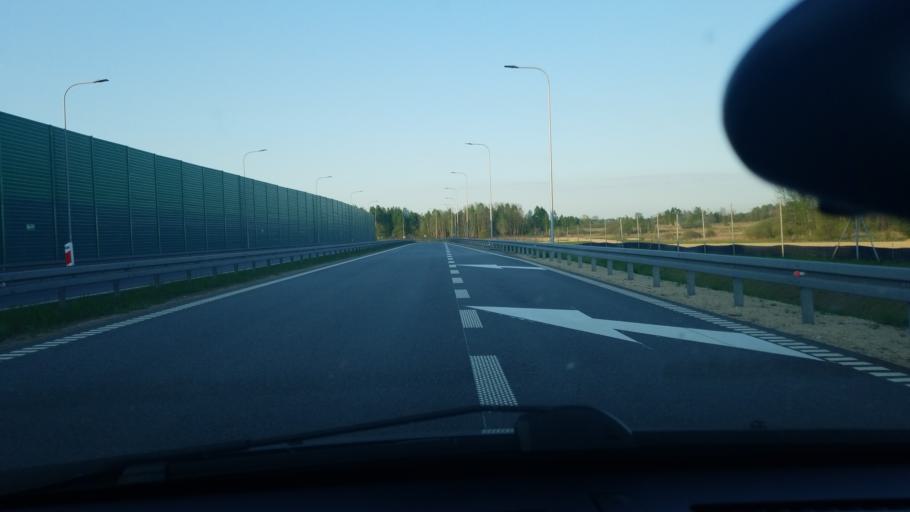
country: PL
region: Silesian Voivodeship
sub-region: Powiat czestochowski
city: Blachownia
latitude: 50.7791
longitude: 19.0086
